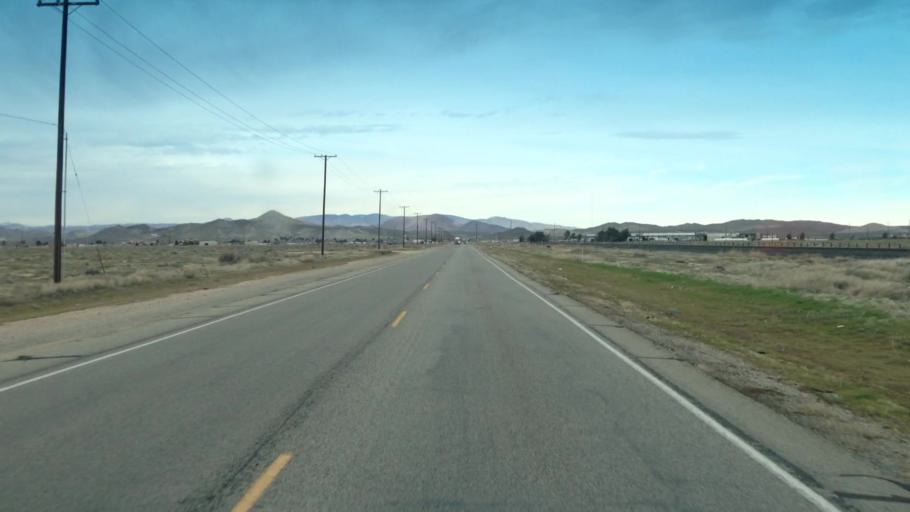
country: US
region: California
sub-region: Kern County
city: Rosamond
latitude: 34.8264
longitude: -118.1570
